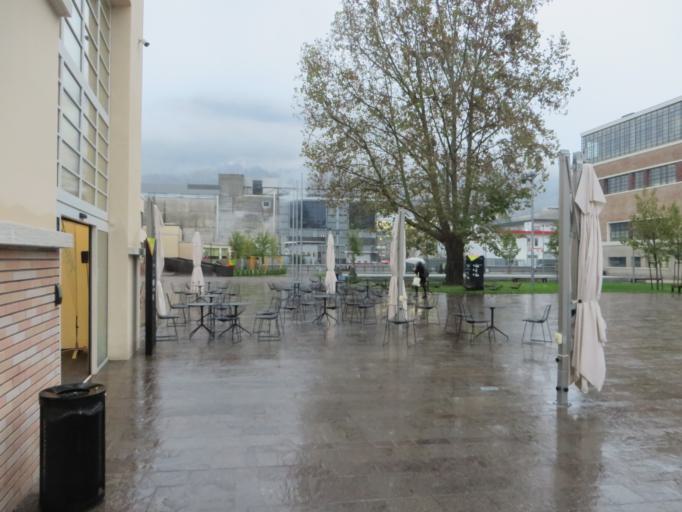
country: IT
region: Trentino-Alto Adige
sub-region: Bolzano
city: Bolzano
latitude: 46.4791
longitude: 11.3322
